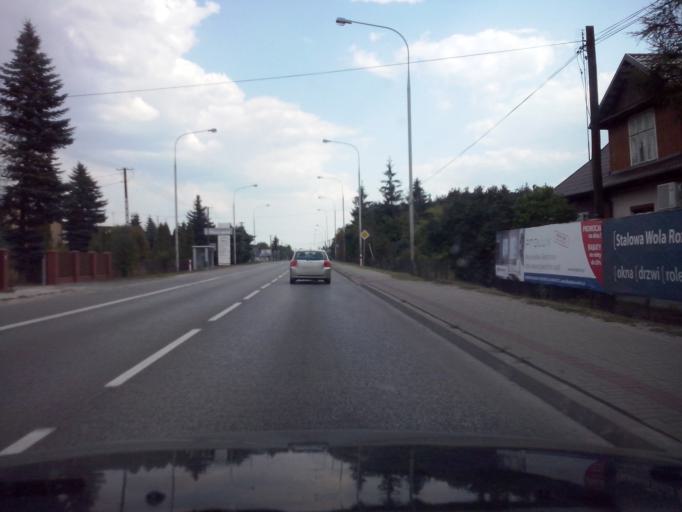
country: PL
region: Subcarpathian Voivodeship
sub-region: Powiat stalowowolski
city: Pysznica
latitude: 50.5423
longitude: 22.0884
